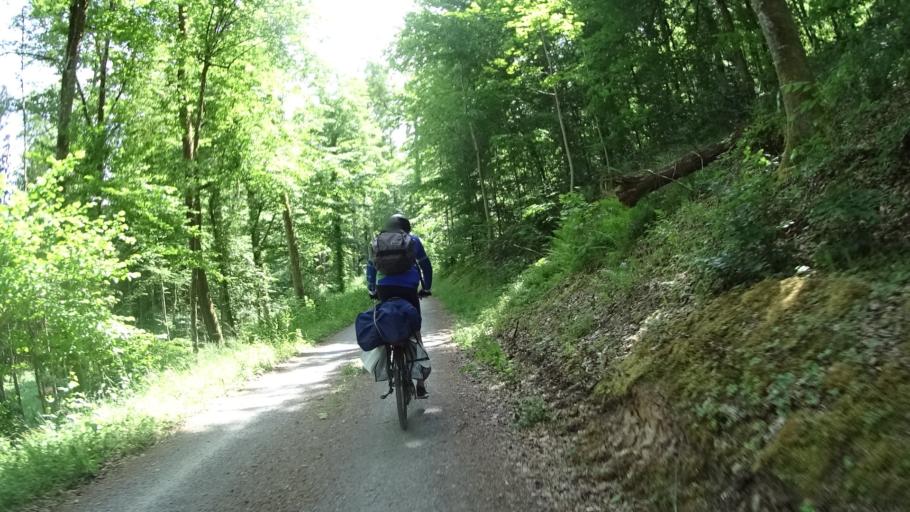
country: DE
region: Bavaria
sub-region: Regierungsbezirk Unterfranken
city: Neunkirchen
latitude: 49.6585
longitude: 9.4269
